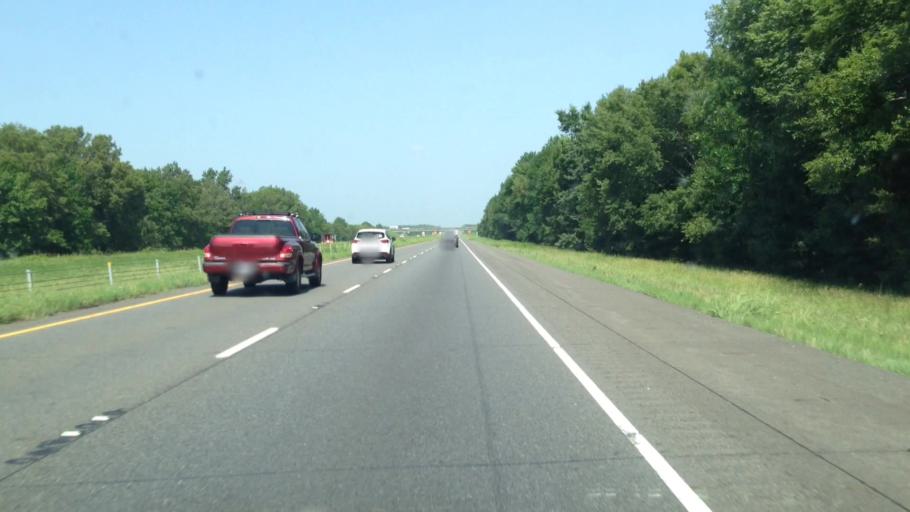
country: US
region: Louisiana
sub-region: Richland Parish
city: Delhi
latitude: 32.4361
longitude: -91.4491
